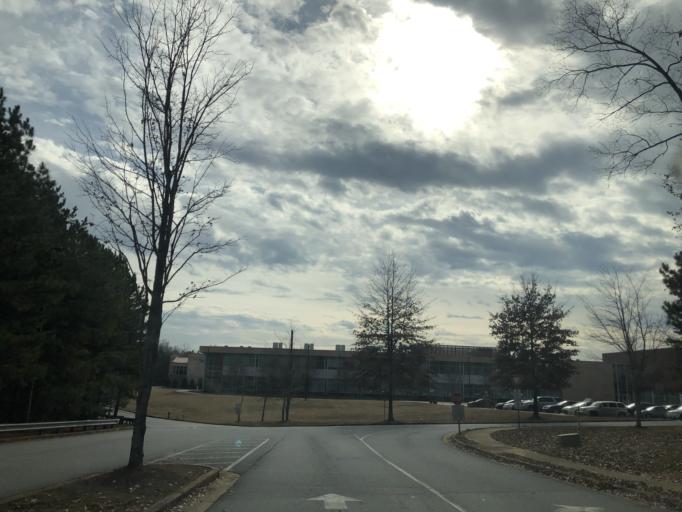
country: US
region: Georgia
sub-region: DeKalb County
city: Pine Mountain
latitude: 33.6628
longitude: -84.1978
